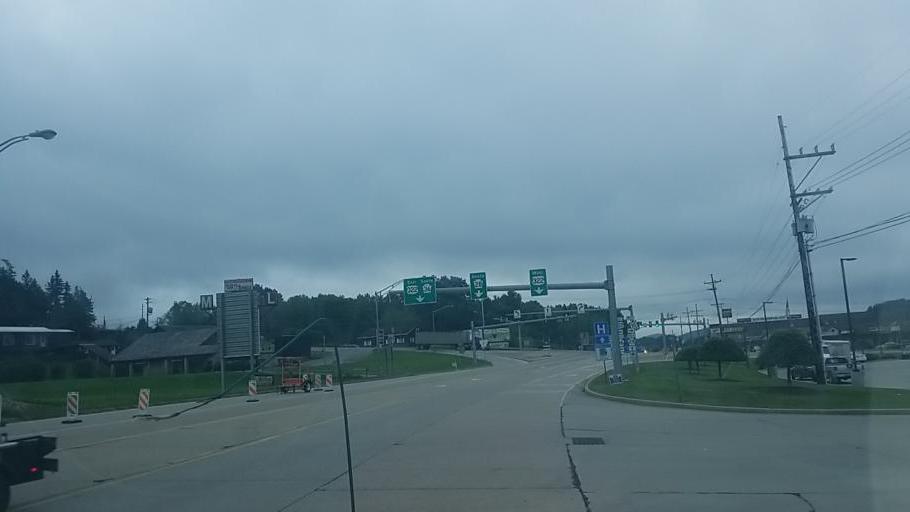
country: US
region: Pennsylvania
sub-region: Jefferson County
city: Brookville
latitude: 41.1646
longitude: -79.0976
